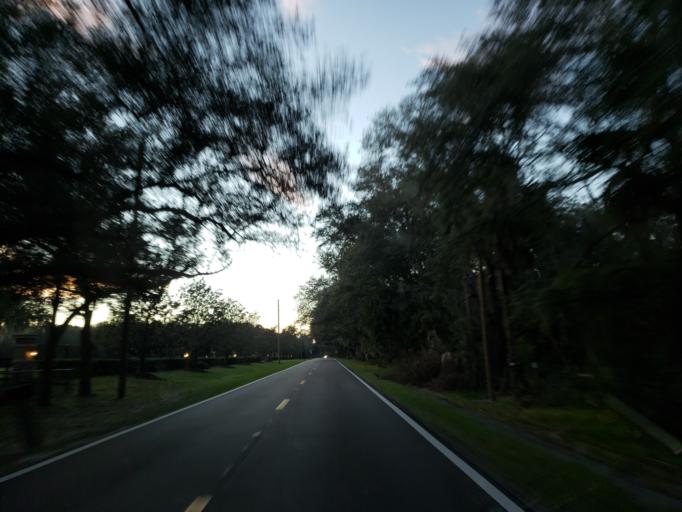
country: US
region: Florida
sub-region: Hillsborough County
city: Boyette
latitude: 27.8214
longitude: -82.2091
